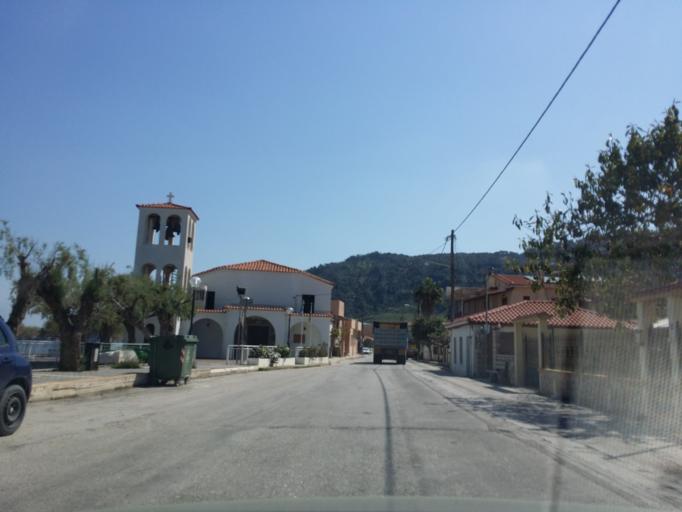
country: GR
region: West Greece
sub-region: Nomos Achaias
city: Aiyira
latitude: 38.1312
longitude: 22.4111
